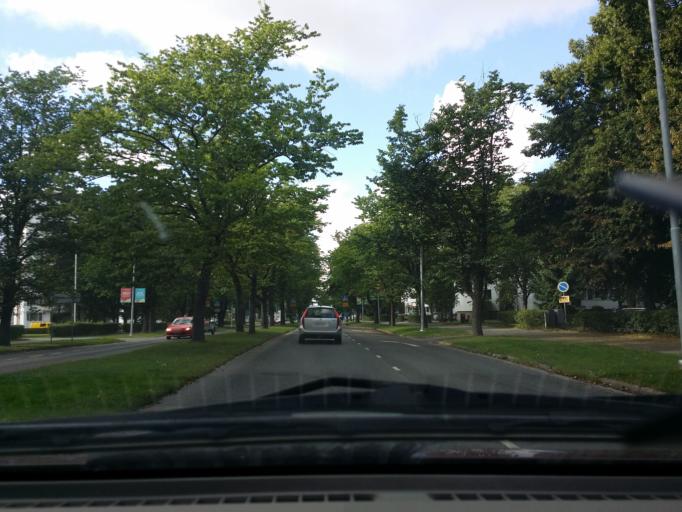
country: FI
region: Satakunta
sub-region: Pori
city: Pori
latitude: 61.4791
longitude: 21.7882
